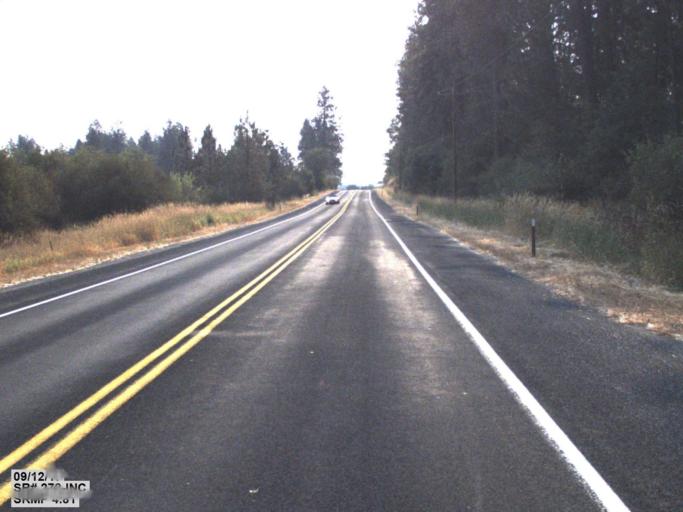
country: US
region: Idaho
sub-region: Benewah County
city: Plummer
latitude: 47.4372
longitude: -117.0541
